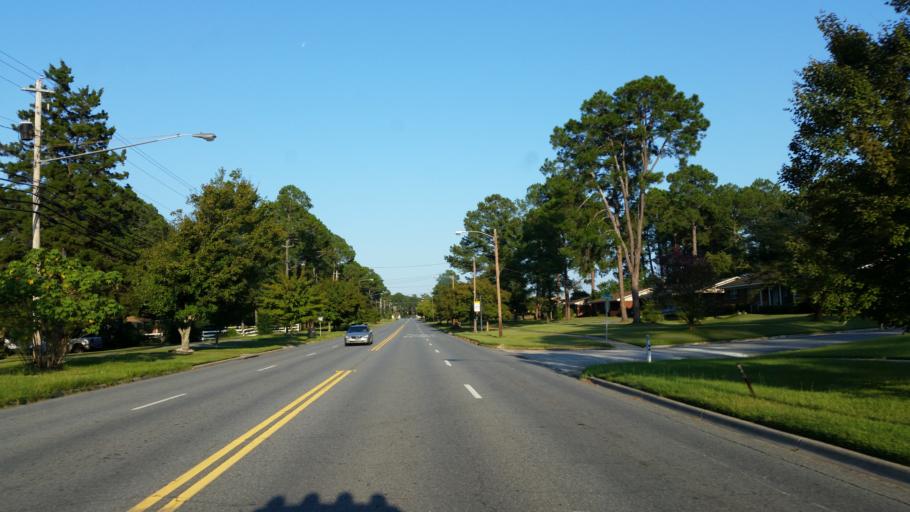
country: US
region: Georgia
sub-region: Tift County
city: Tifton
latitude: 31.4633
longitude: -83.5255
